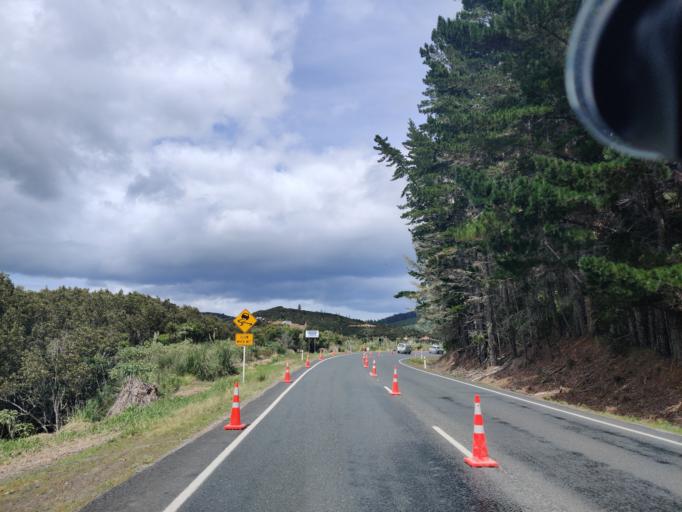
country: NZ
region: Northland
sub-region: Far North District
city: Taipa
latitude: -35.0115
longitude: 173.5553
